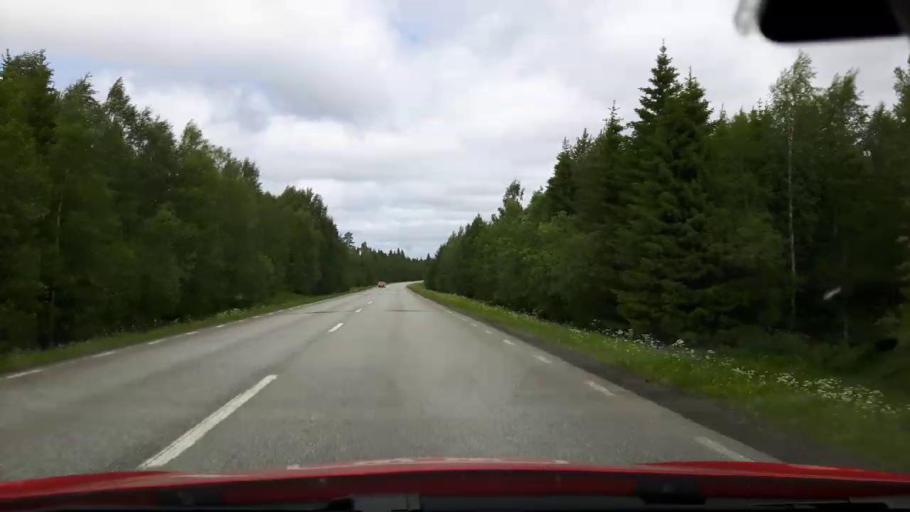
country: SE
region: Jaemtland
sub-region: Krokoms Kommun
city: Krokom
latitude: 63.3725
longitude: 14.5069
